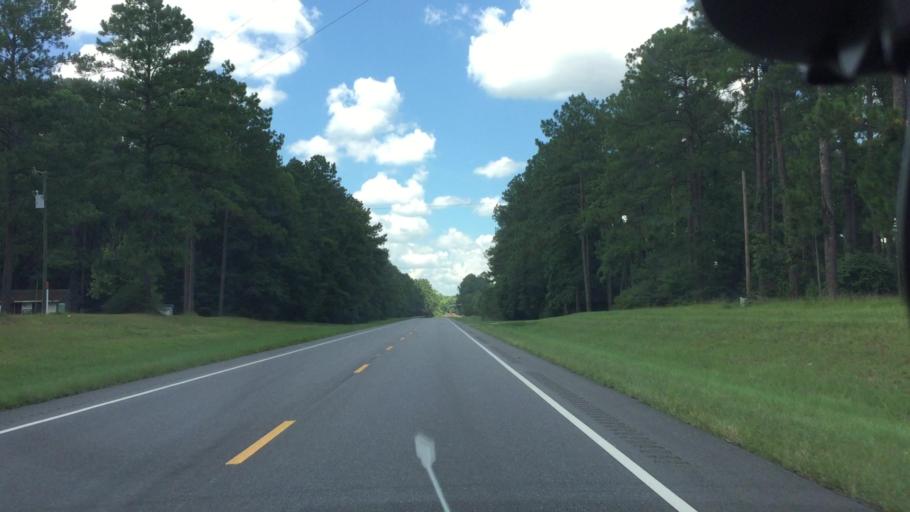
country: US
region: Alabama
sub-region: Coffee County
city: New Brockton
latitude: 31.4821
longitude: -85.9099
